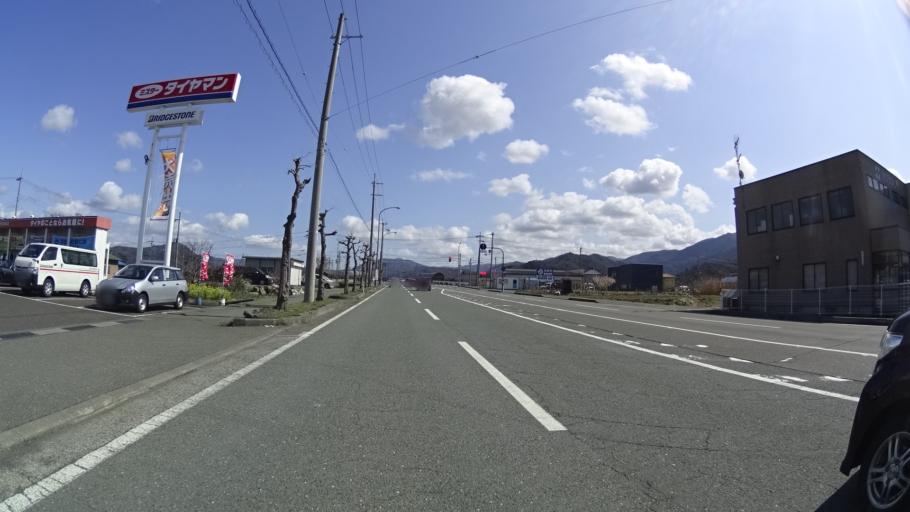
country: JP
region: Fukui
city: Obama
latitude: 35.4939
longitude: 135.7596
